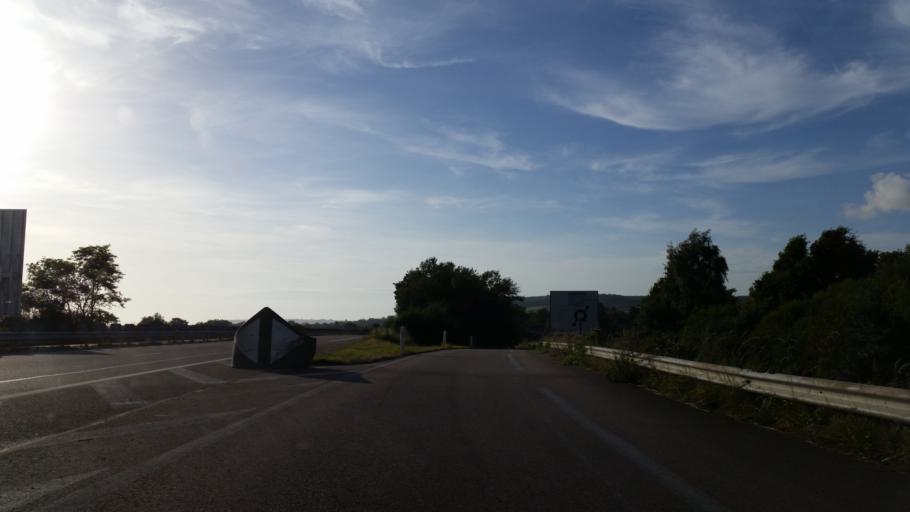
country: FR
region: Lower Normandy
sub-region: Departement du Calvados
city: Saint-Gatien-des-Bois
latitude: 49.2987
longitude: 0.1889
